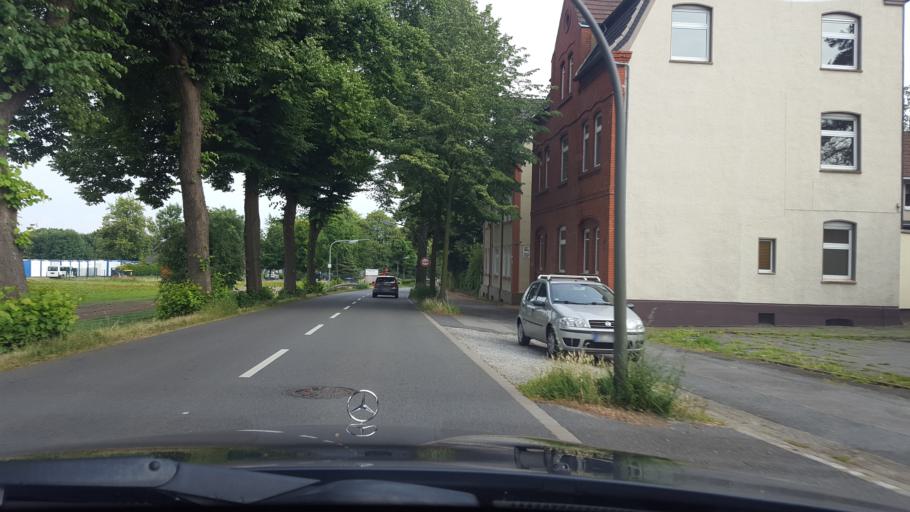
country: DE
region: North Rhine-Westphalia
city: Oer-Erkenschwick
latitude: 51.6150
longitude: 7.2581
